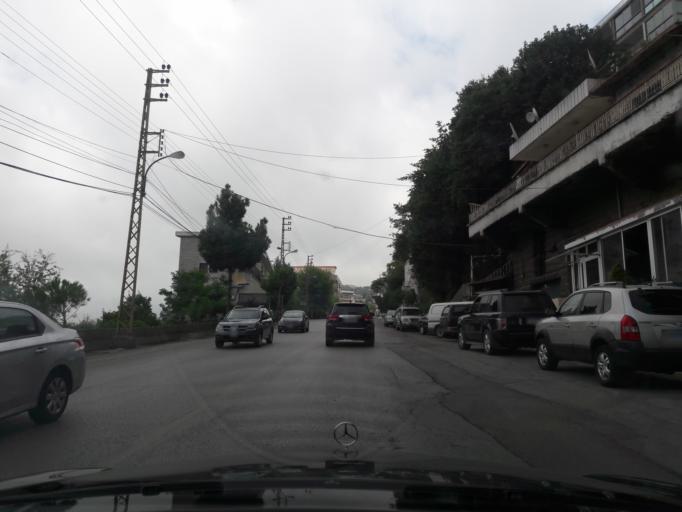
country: LB
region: Mont-Liban
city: Djounie
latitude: 33.9180
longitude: 35.6715
